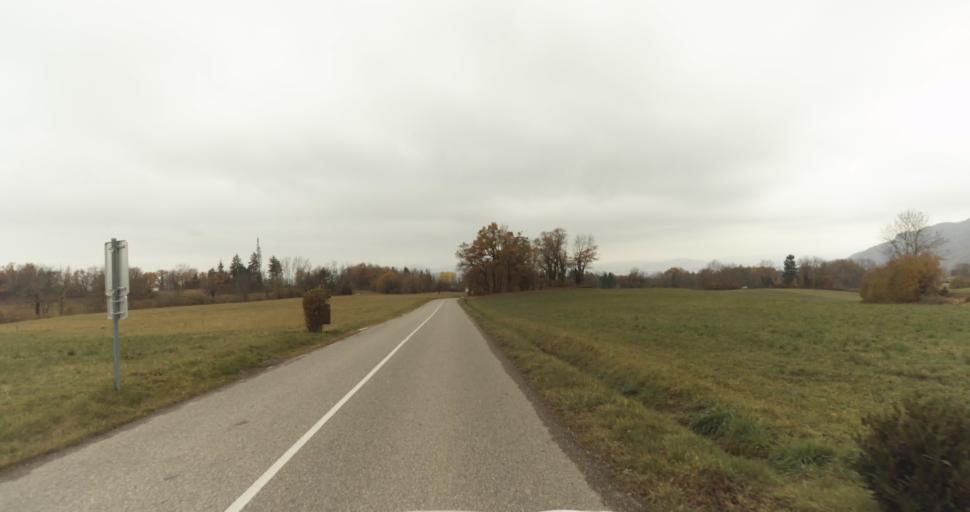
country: FR
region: Rhone-Alpes
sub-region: Departement de la Haute-Savoie
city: Seynod
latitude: 45.8496
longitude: 6.0847
